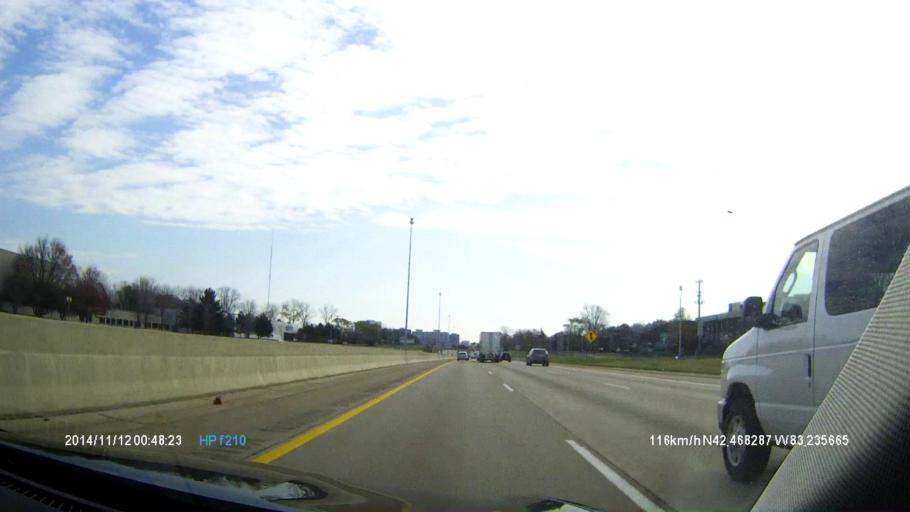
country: US
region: Michigan
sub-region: Oakland County
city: Southfield
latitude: 42.4682
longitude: -83.2355
